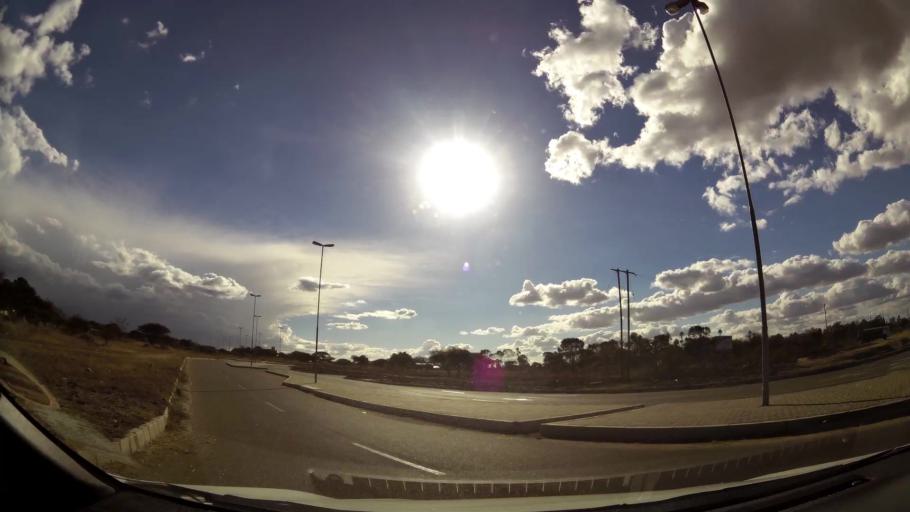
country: ZA
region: Limpopo
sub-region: Capricorn District Municipality
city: Polokwane
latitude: -23.9355
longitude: 29.4488
